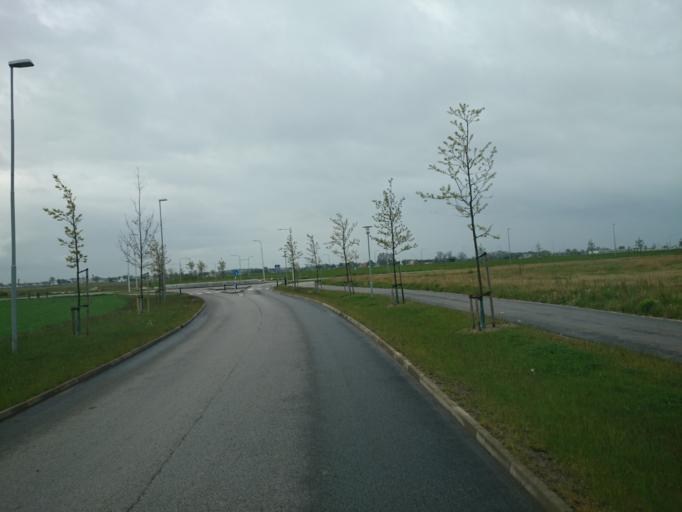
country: SE
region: Skane
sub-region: Malmo
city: Bunkeflostrand
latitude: 55.5441
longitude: 12.9276
